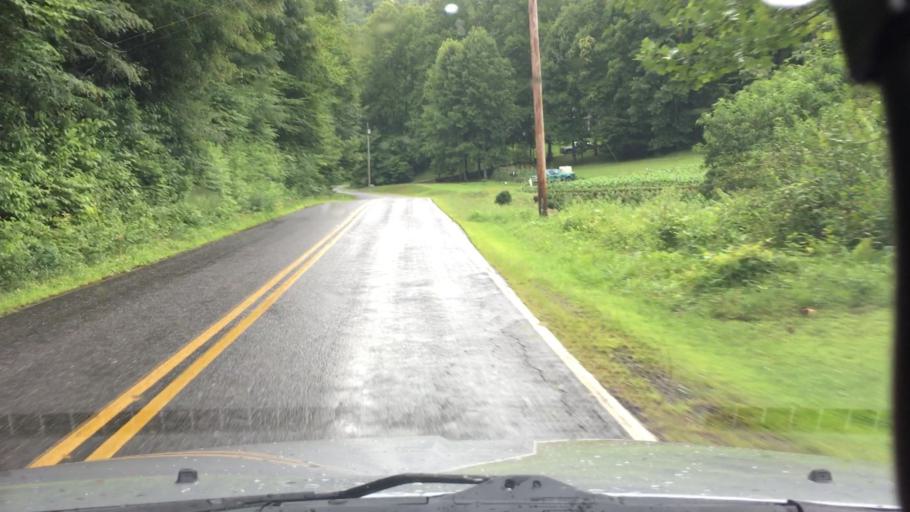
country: US
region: North Carolina
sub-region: Madison County
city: Mars Hill
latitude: 35.9136
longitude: -82.4786
